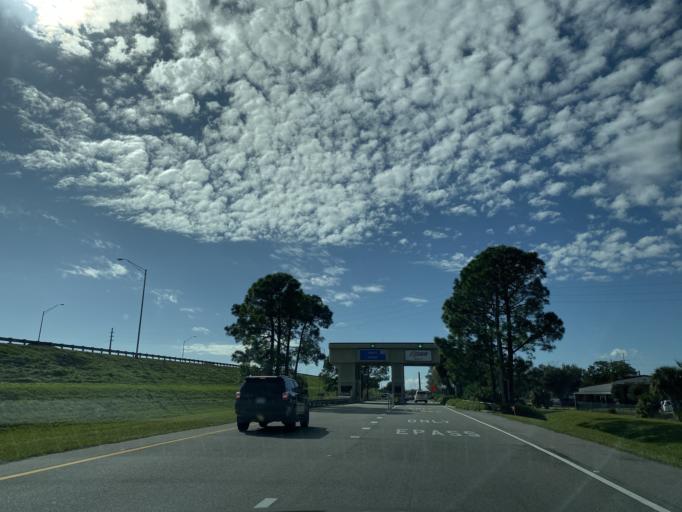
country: US
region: Florida
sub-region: Orange County
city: Meadow Woods
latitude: 28.4023
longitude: -81.2423
